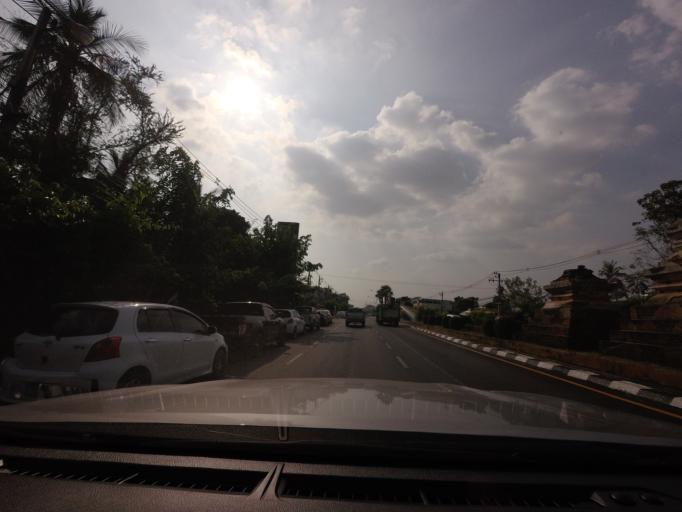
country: TH
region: Sukhothai
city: Sukhothai
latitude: 17.0103
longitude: 99.8335
